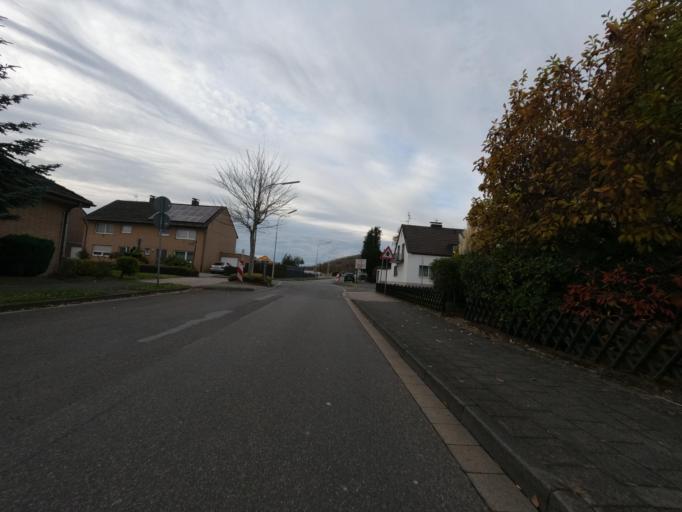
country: DE
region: North Rhine-Westphalia
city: Huckelhoven
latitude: 51.0491
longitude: 6.2192
